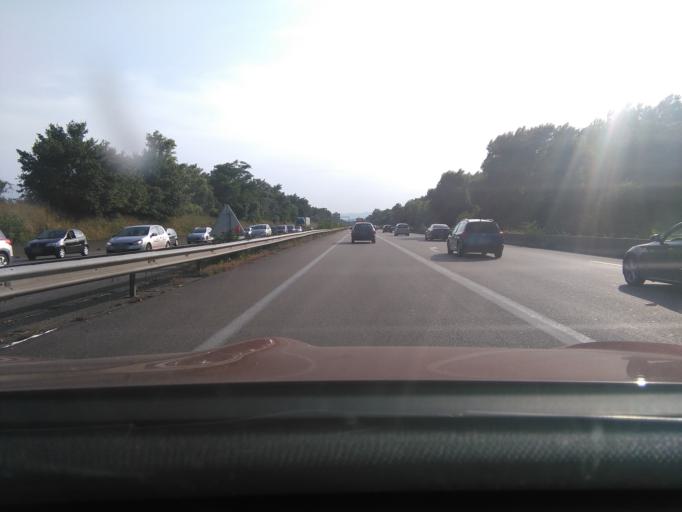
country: FR
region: Rhone-Alpes
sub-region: Departement du Rhone
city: Vaulx-en-Velin
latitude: 45.7940
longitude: 4.9227
